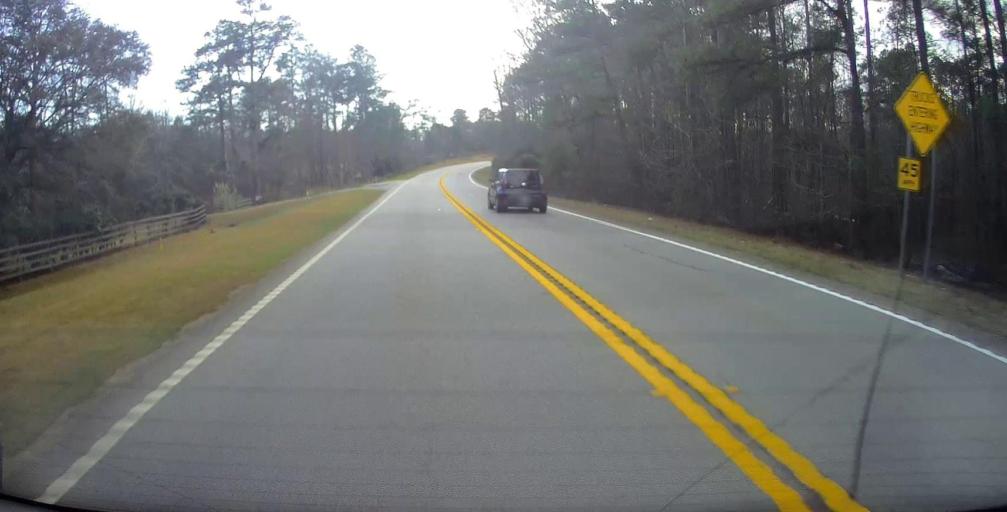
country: US
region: Georgia
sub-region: Harris County
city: Hamilton
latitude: 32.6632
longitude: -84.7635
